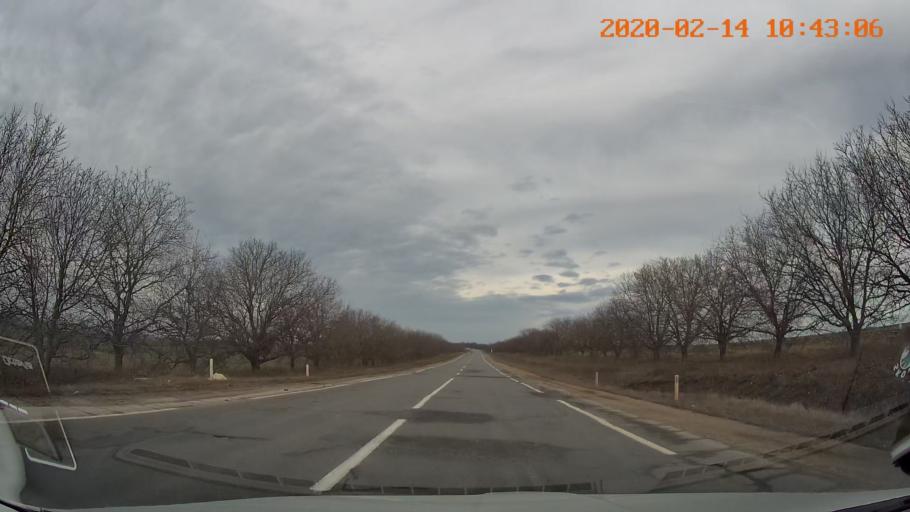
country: MD
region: Riscani
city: Riscani
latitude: 48.0042
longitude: 27.5695
